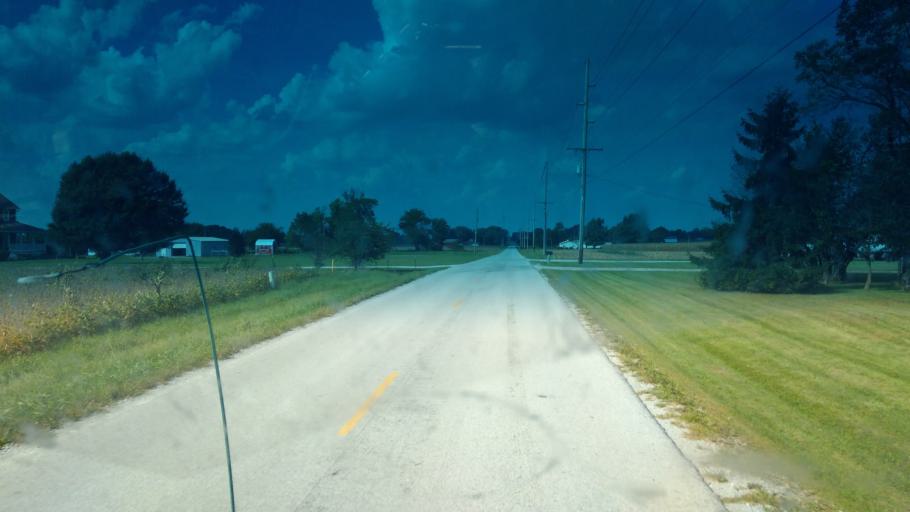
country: US
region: Ohio
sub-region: Hancock County
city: Arlington
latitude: 40.7716
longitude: -83.6521
